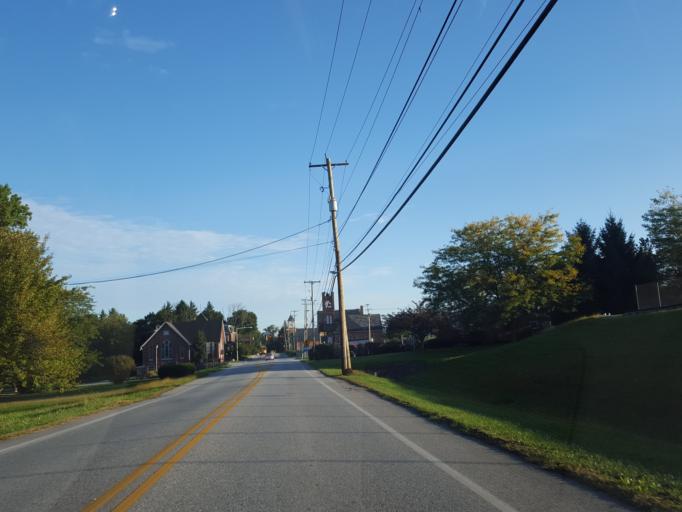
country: US
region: Pennsylvania
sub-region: York County
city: Windsor
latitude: 39.9264
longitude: -76.6065
